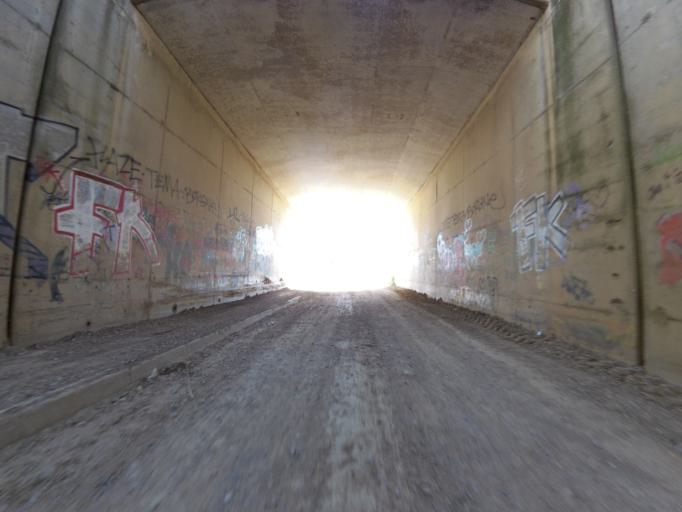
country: FR
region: Languedoc-Roussillon
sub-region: Departement du Gard
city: Gallargues-le-Montueux
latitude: 43.7244
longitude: 4.1571
